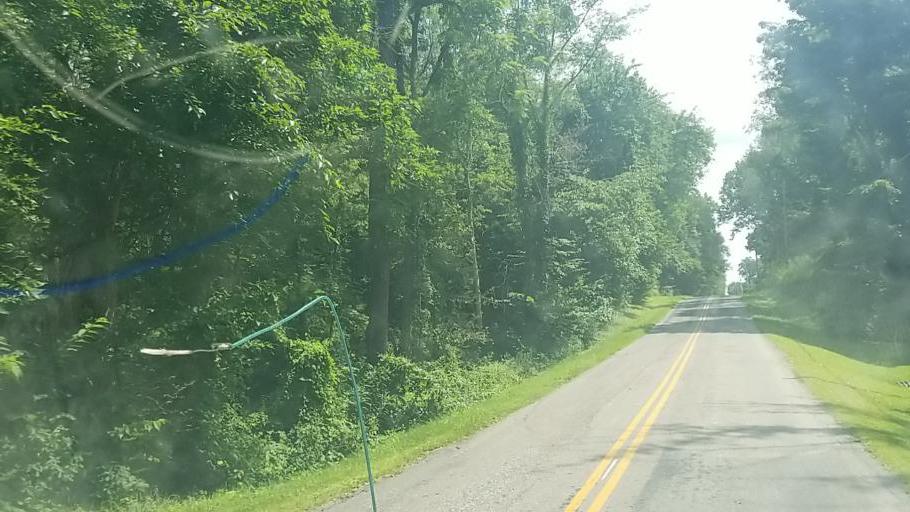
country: US
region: Ohio
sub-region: Wayne County
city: West Salem
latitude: 41.0142
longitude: -82.0757
